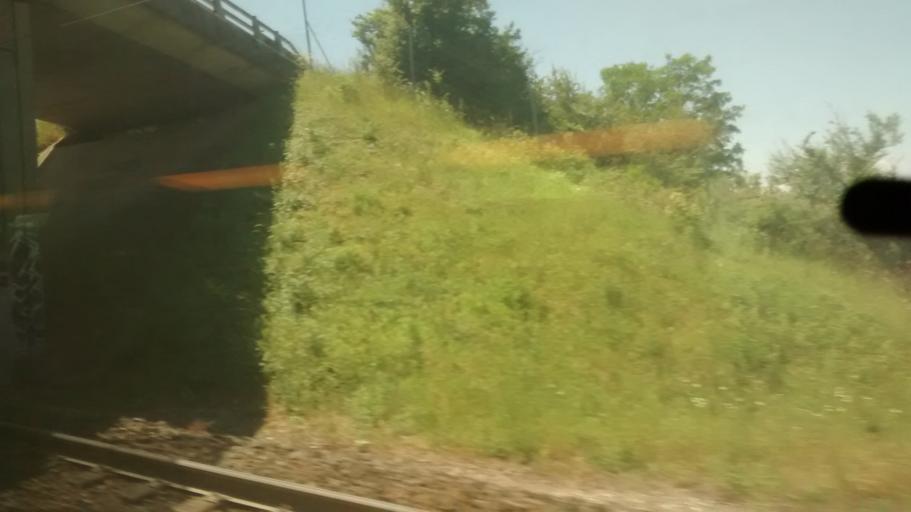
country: FR
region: Rhone-Alpes
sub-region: Departement du Rhone
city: Sathonay-Village
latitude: 45.8417
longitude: 4.8903
